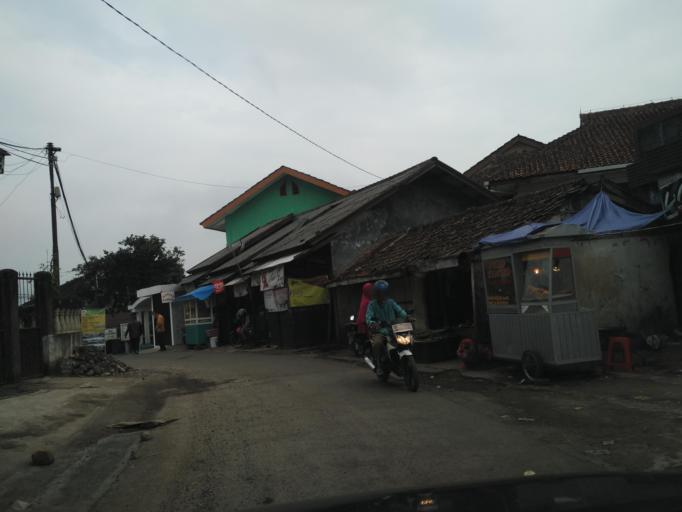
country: ID
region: West Java
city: Caringin
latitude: -6.7009
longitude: 107.0365
